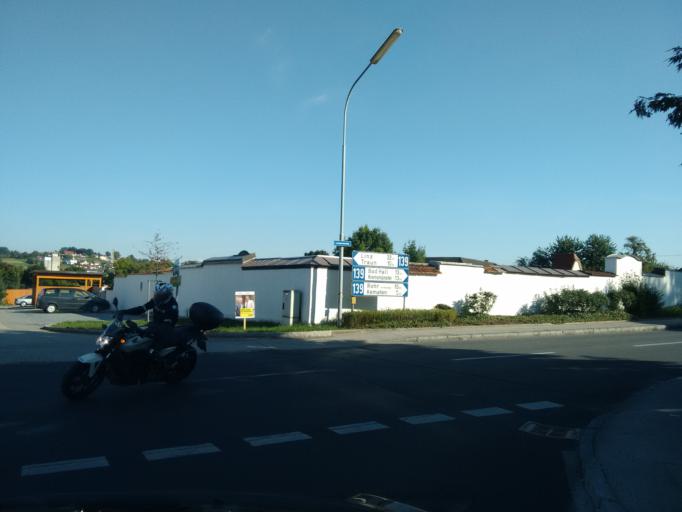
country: AT
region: Upper Austria
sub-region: Politischer Bezirk Linz-Land
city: Traun
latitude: 48.1410
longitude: 14.2282
